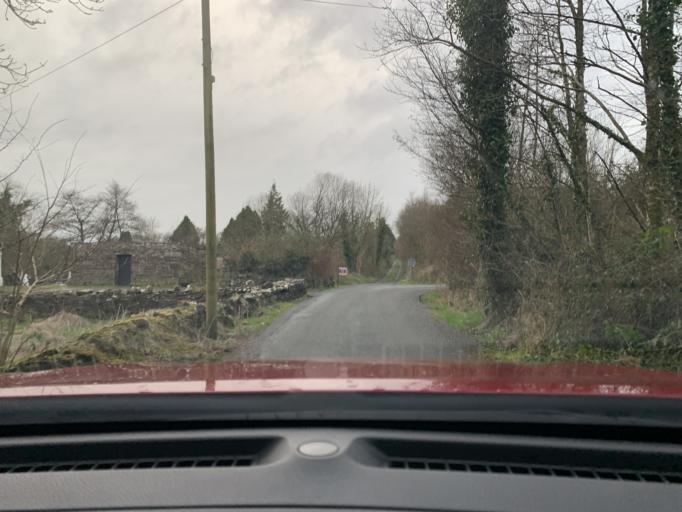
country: IE
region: Connaught
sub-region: Roscommon
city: Boyle
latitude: 53.9791
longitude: -8.4172
